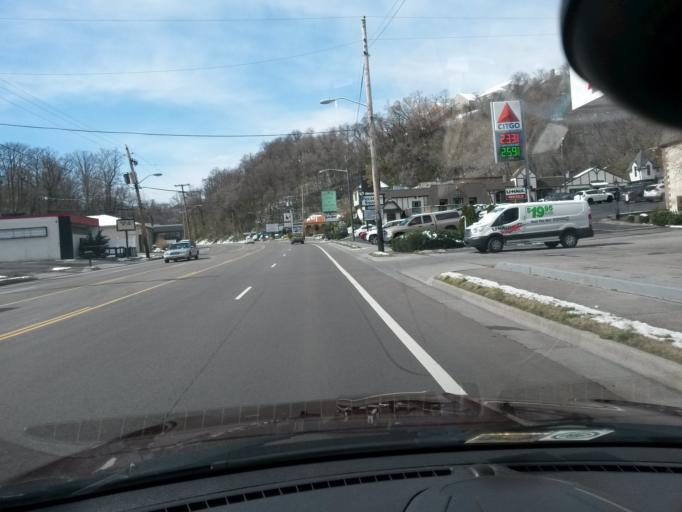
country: US
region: Virginia
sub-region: City of Roanoke
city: Cedar Bluff
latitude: 37.2445
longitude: -79.9628
